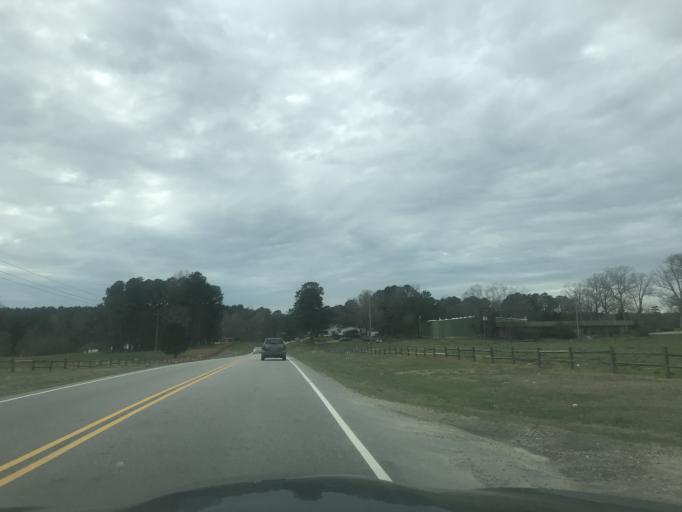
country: US
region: North Carolina
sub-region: Franklin County
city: Franklinton
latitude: 36.0955
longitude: -78.4170
